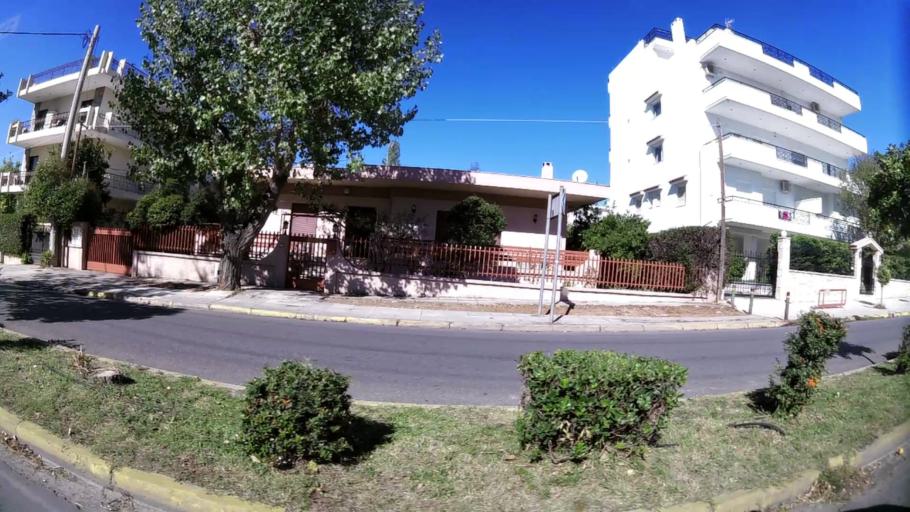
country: GR
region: Attica
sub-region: Nomarchia Athinas
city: Kifisia
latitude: 38.0871
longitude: 23.8014
